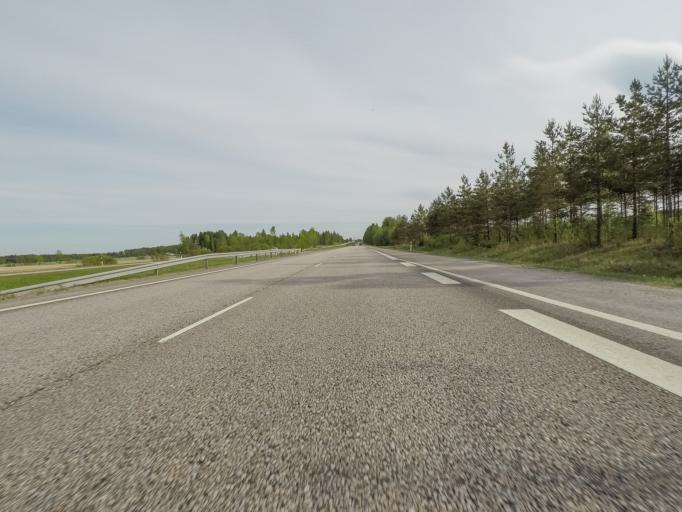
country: FI
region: Uusimaa
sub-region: Helsinki
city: Nurmijaervi
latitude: 60.5132
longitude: 24.8472
